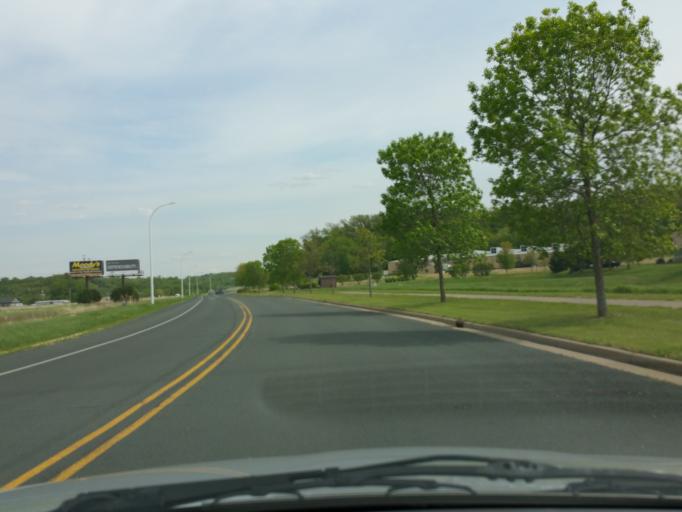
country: US
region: Wisconsin
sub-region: Pierce County
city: River Falls
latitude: 44.8866
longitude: -92.6295
